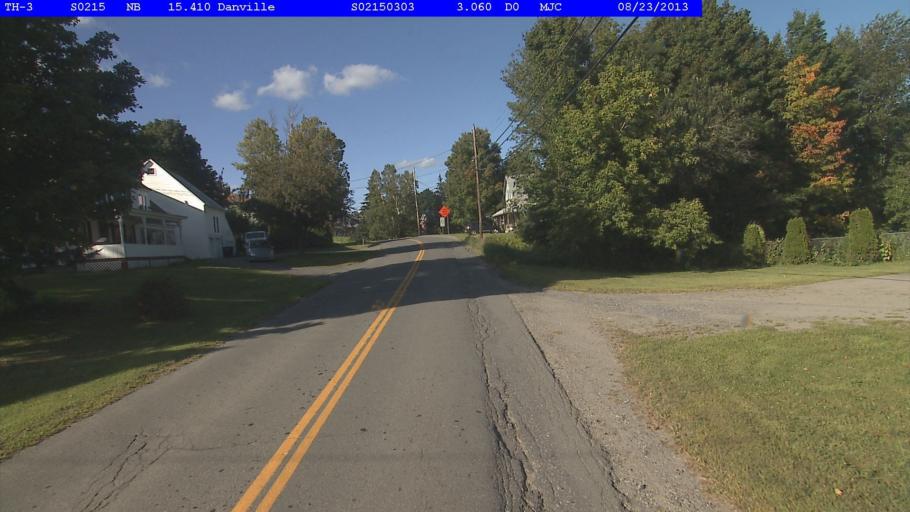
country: US
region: Vermont
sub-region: Caledonia County
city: Saint Johnsbury
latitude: 44.4084
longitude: -72.1401
